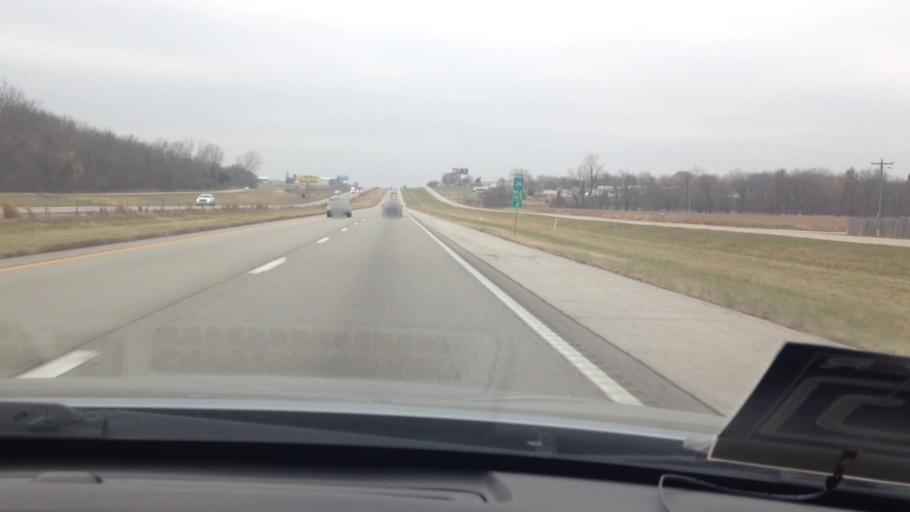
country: US
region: Missouri
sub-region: Cass County
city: Peculiar
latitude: 38.7011
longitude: -94.4341
